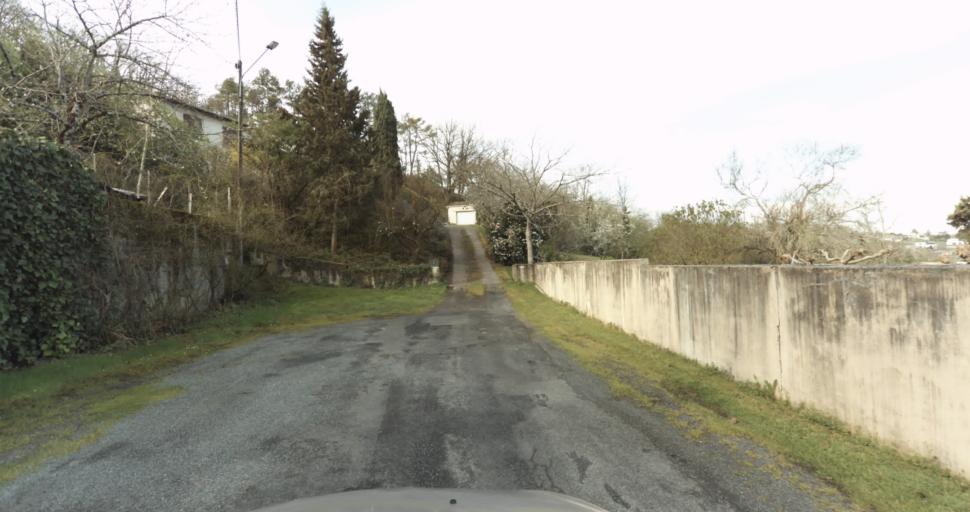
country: FR
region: Midi-Pyrenees
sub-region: Departement du Tarn
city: Puygouzon
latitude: 43.9041
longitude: 2.1747
